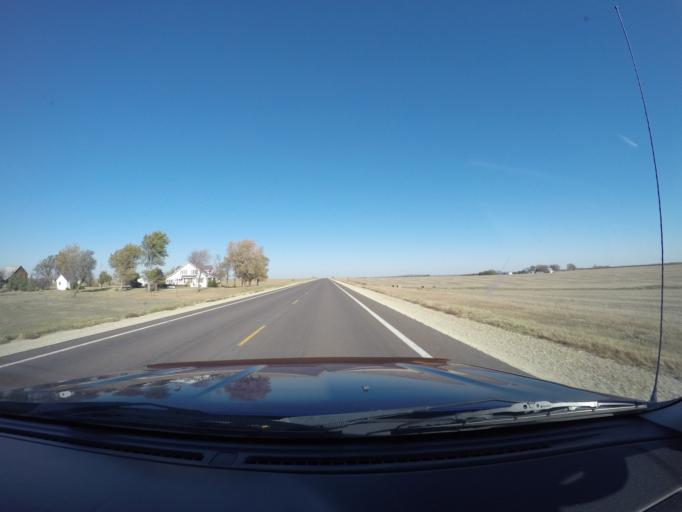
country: US
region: Kansas
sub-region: Marshall County
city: Blue Rapids
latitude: 39.6349
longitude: -96.7503
